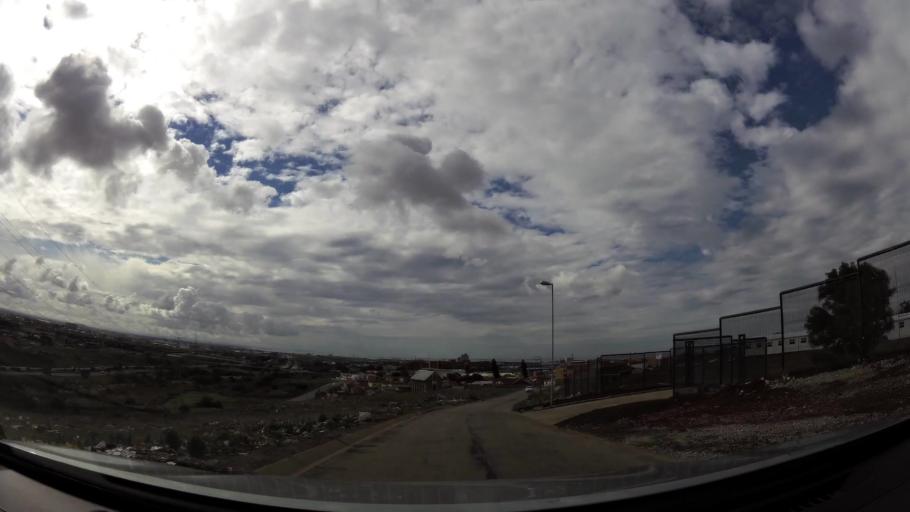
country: ZA
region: Eastern Cape
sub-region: Nelson Mandela Bay Metropolitan Municipality
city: Port Elizabeth
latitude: -33.9284
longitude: 25.5610
